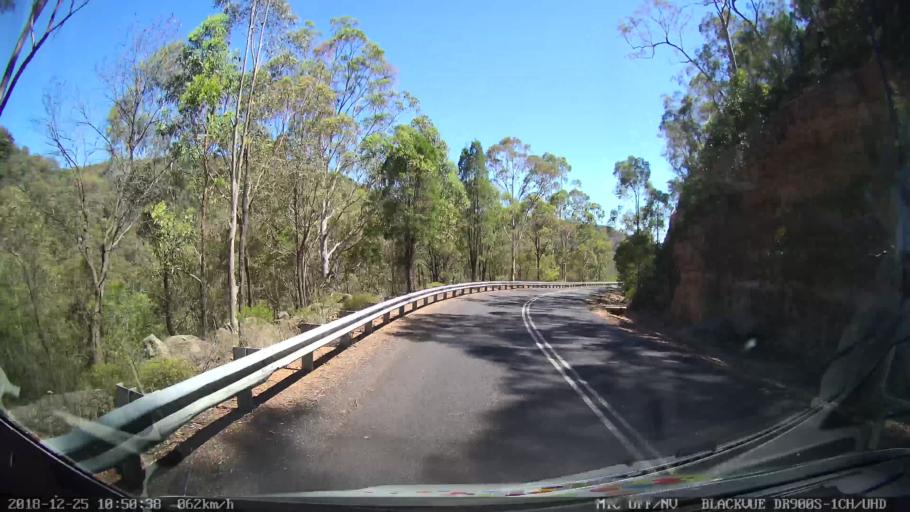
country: AU
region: New South Wales
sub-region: Upper Hunter Shire
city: Merriwa
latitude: -32.4442
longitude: 150.2677
